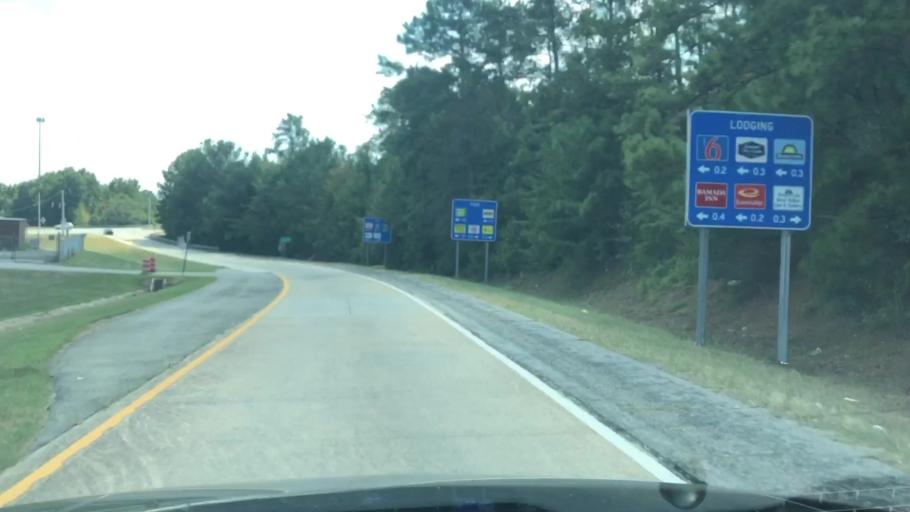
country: US
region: Georgia
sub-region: Bibb County
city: West Point
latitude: 32.8112
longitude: -83.7274
